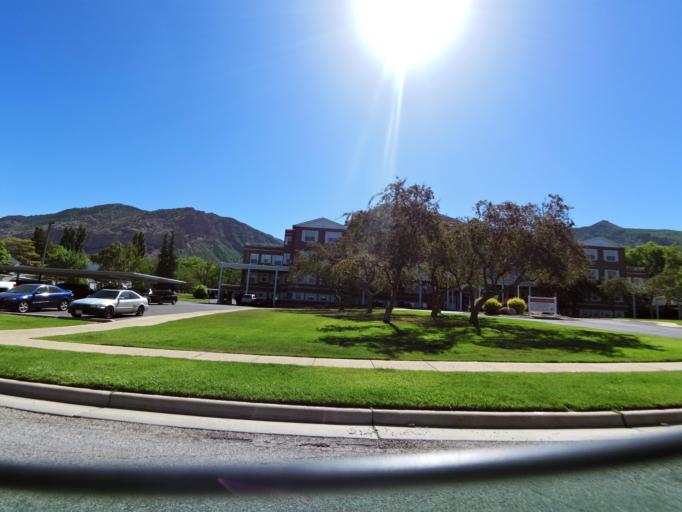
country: US
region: Utah
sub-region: Weber County
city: Ogden
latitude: 41.2099
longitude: -111.9429
